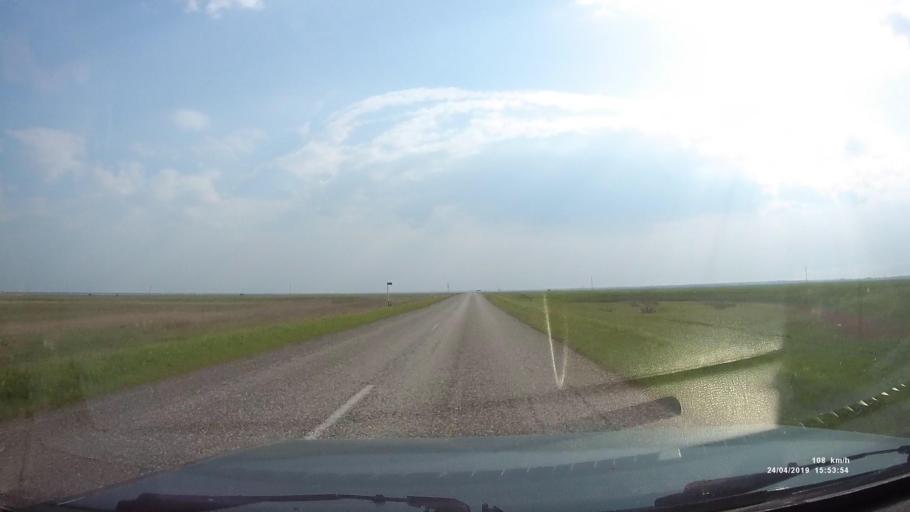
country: RU
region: Kalmykiya
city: Yashalta
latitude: 46.5921
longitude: 42.5695
